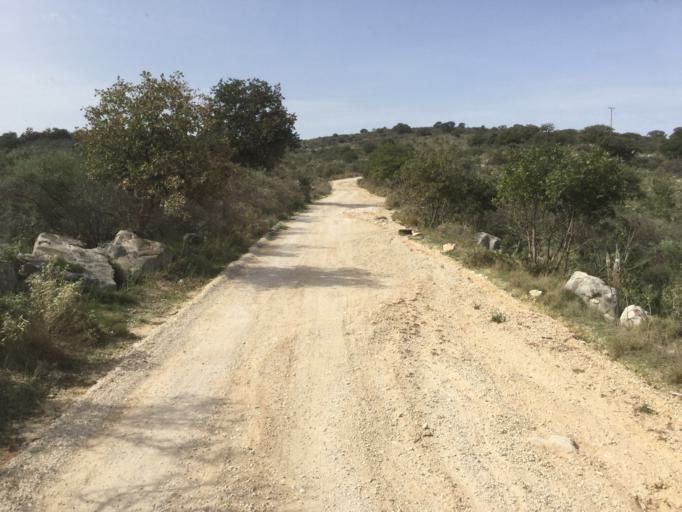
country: GR
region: West Greece
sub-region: Nomos Achaias
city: Lapas
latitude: 38.1822
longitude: 21.3813
